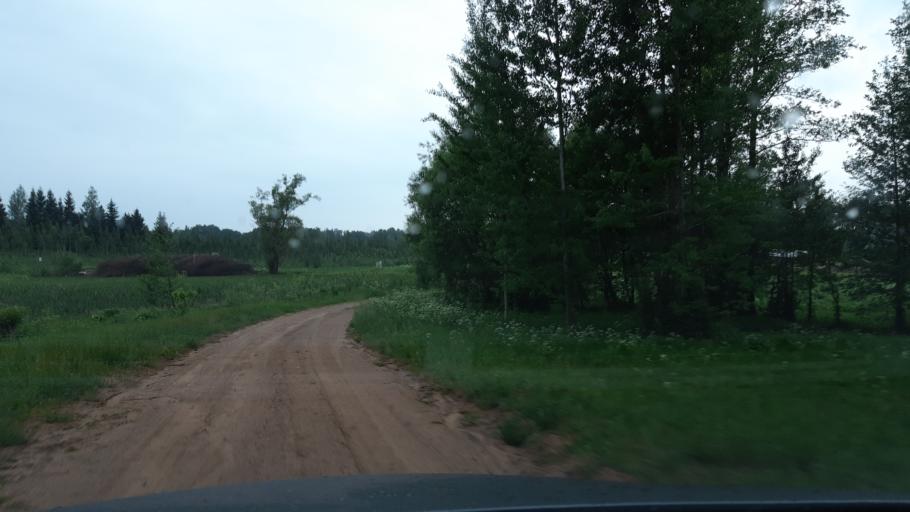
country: LT
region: Utenos apskritis
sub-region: Anyksciai
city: Anyksciai
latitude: 55.4469
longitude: 25.2075
